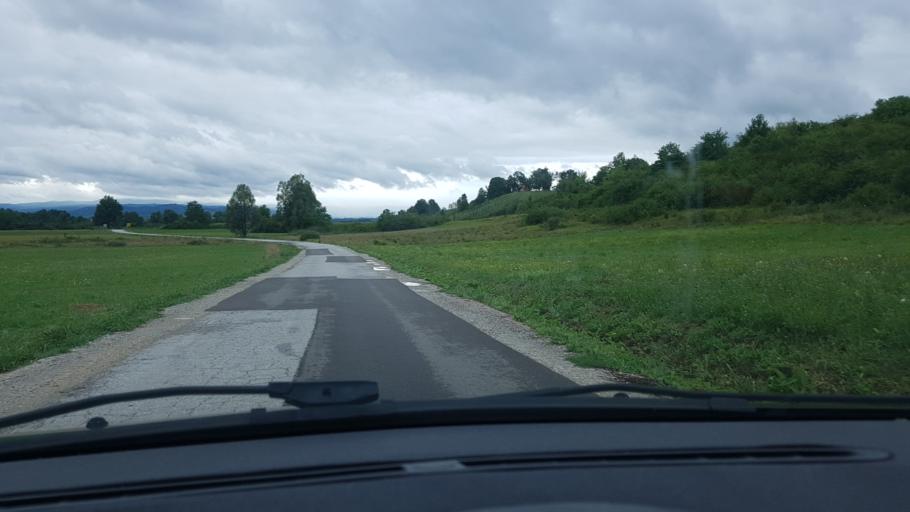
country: HR
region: Karlovacka
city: Ozalj
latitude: 45.5801
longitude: 15.5420
